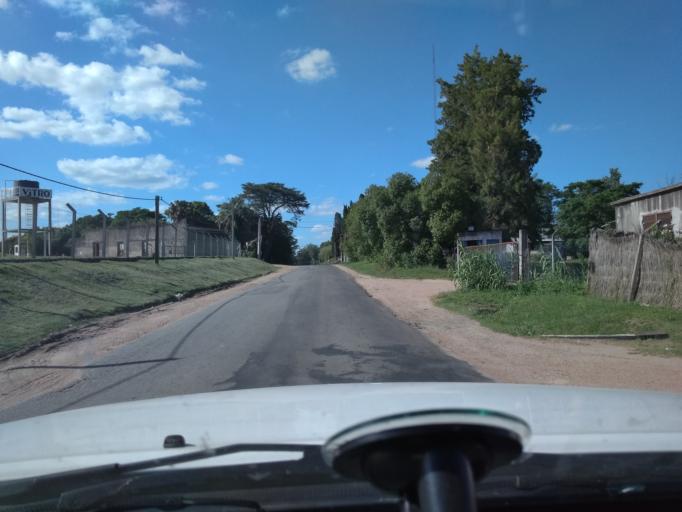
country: UY
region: Canelones
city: La Paz
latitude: -34.8029
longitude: -56.2100
